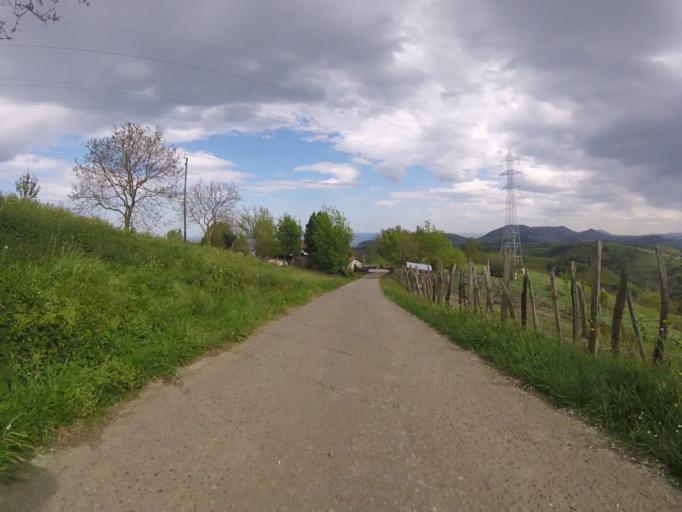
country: ES
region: Basque Country
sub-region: Provincia de Guipuzcoa
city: Zarautz
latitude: 43.2568
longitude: -2.1757
